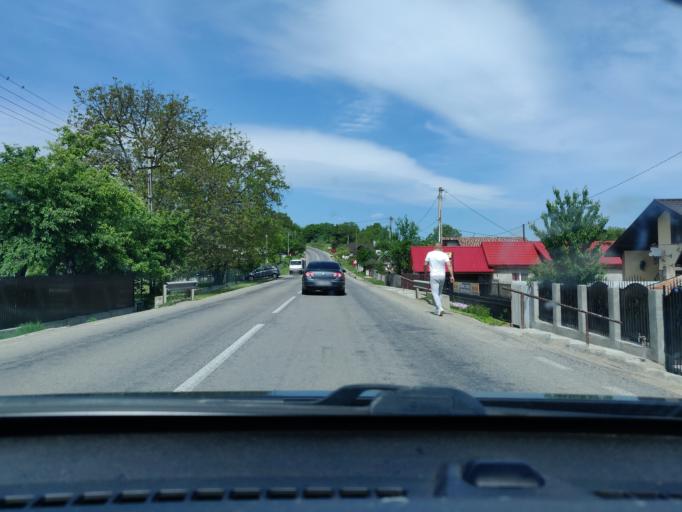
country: RO
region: Vrancea
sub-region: Comuna Vidra
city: Burca
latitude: 45.9073
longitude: 26.9605
